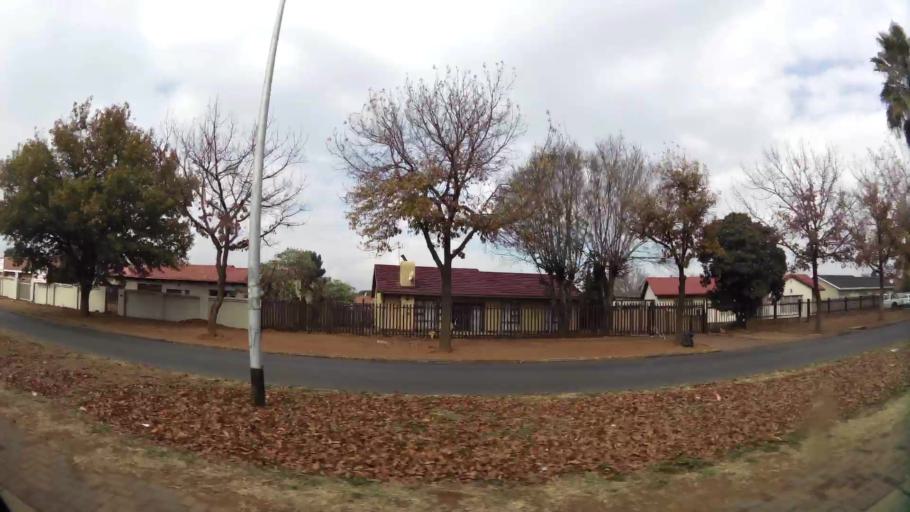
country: ZA
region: Gauteng
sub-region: Sedibeng District Municipality
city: Vanderbijlpark
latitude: -26.6958
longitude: 27.8518
